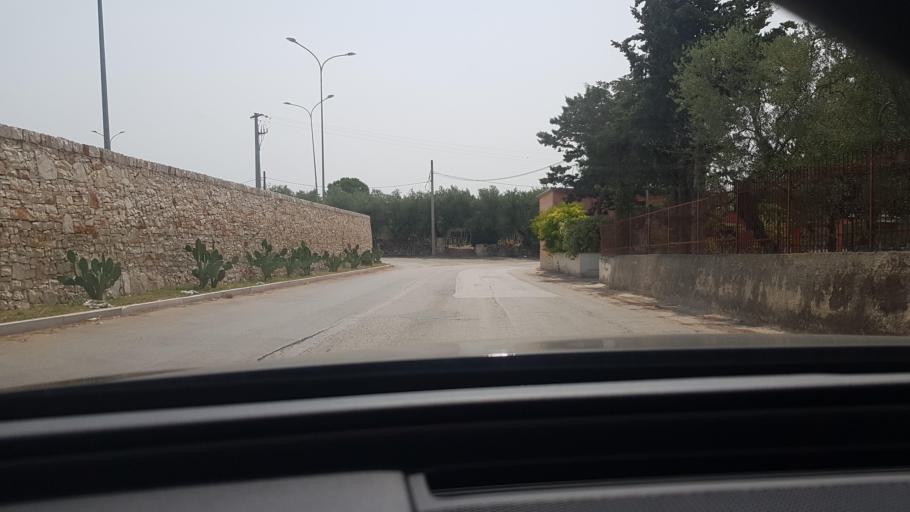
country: IT
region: Apulia
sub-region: Provincia di Barletta - Andria - Trani
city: Andria
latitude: 41.2291
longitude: 16.2686
